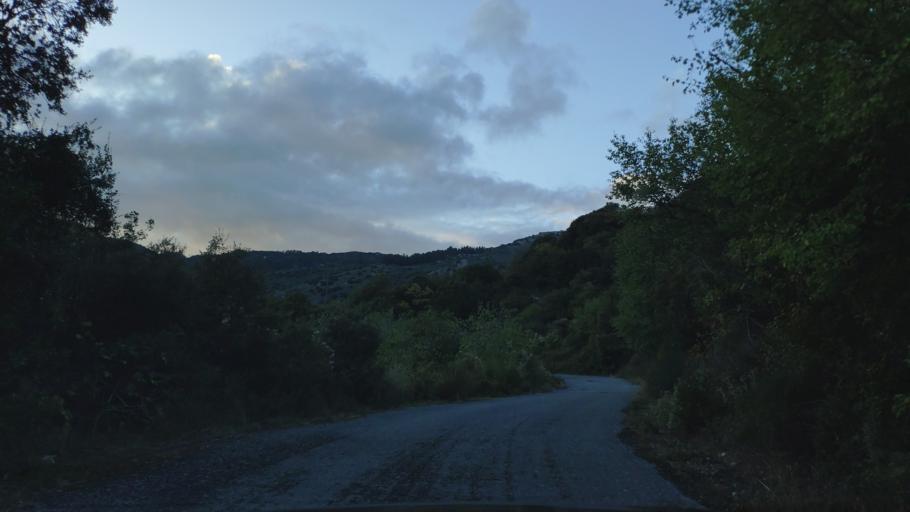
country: GR
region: Peloponnese
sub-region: Nomos Arkadias
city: Dimitsana
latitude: 37.5861
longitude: 22.0405
